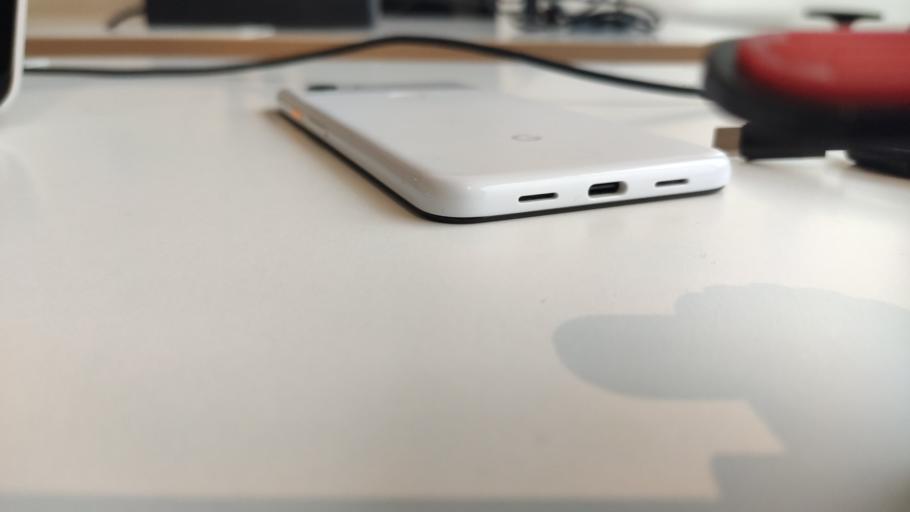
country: RU
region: Moskovskaya
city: Rogachevo
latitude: 56.4329
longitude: 37.1308
